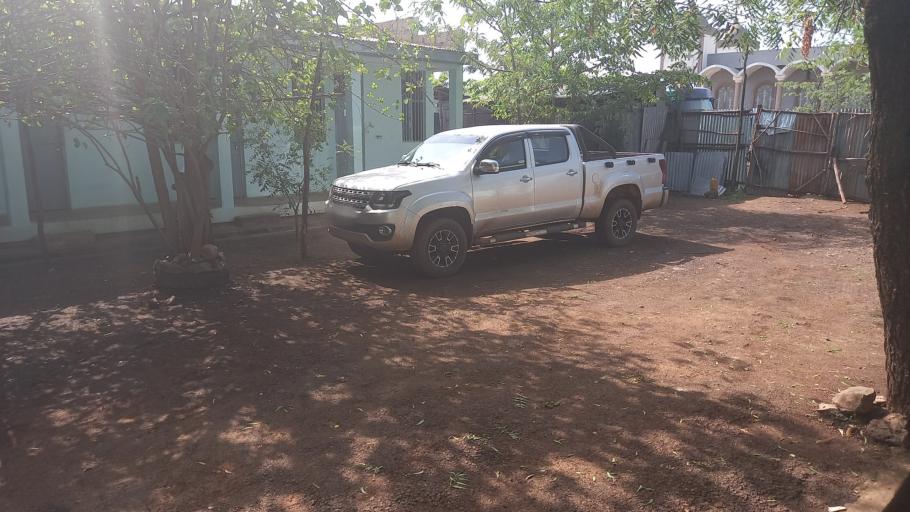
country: ET
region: Southern Nations, Nationalities, and People's Region
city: Bako
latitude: 6.2244
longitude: 36.1259
